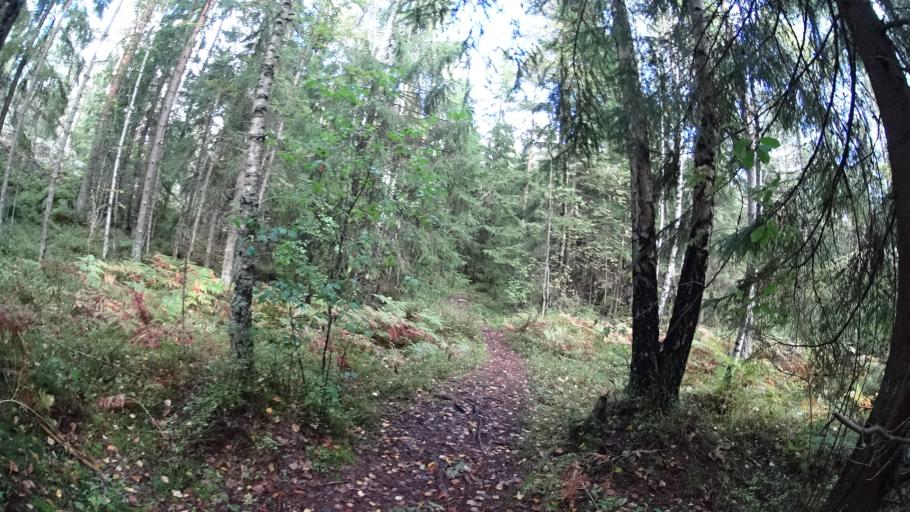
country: FI
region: Uusimaa
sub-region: Helsinki
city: Espoo
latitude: 60.2294
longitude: 24.6821
